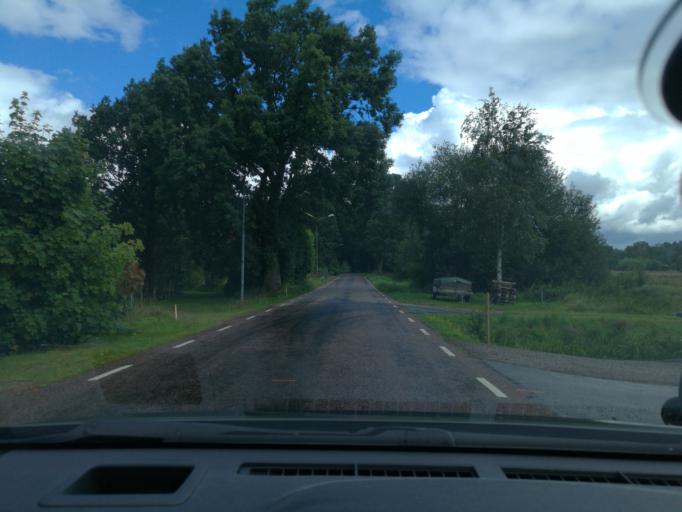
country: SE
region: Skane
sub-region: Eslovs Kommun
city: Stehag
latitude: 55.9056
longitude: 13.4313
